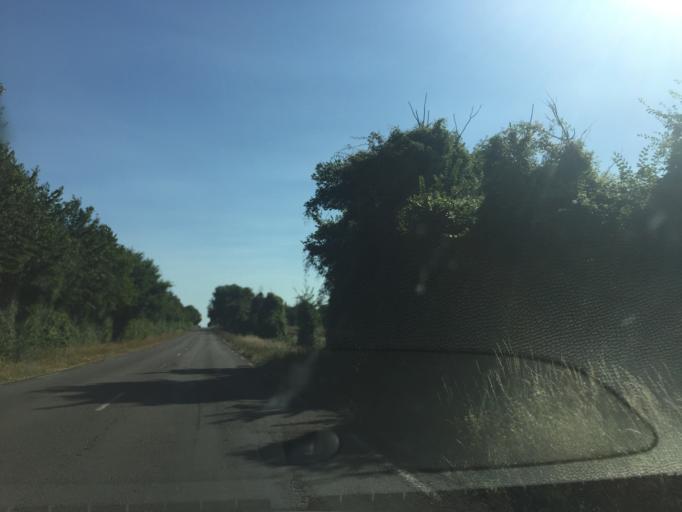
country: FR
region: Poitou-Charentes
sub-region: Departement des Deux-Sevres
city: Melle
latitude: 46.2500
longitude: -0.0997
